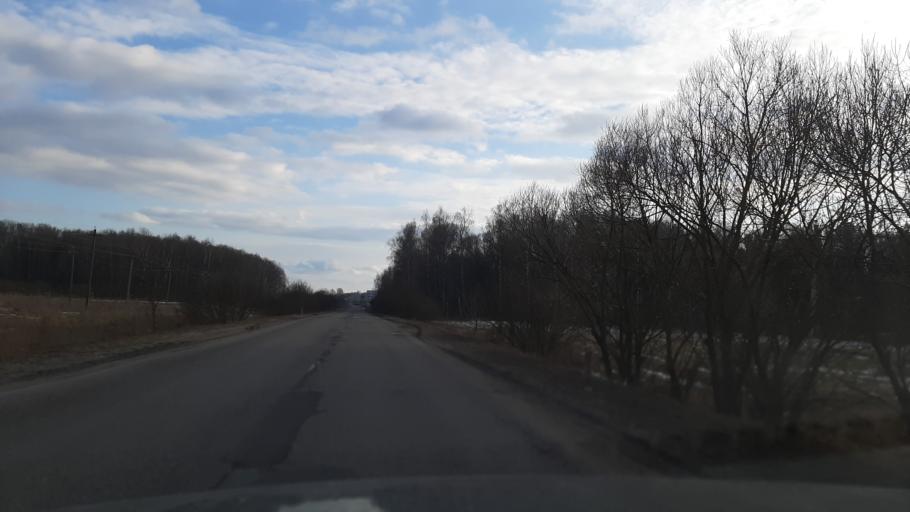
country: RU
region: Ivanovo
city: Novo-Talitsy
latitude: 56.9320
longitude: 40.7346
